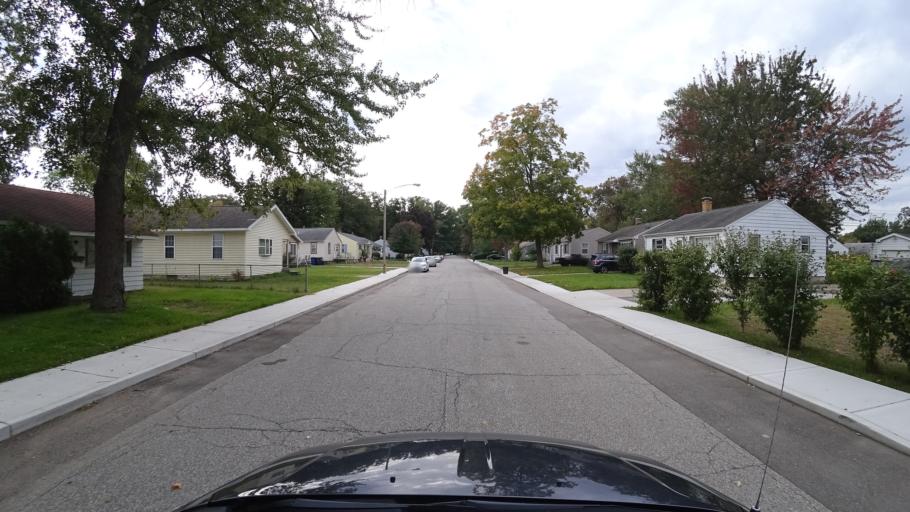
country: US
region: Indiana
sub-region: LaPorte County
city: Michigan City
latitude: 41.6978
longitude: -86.8811
